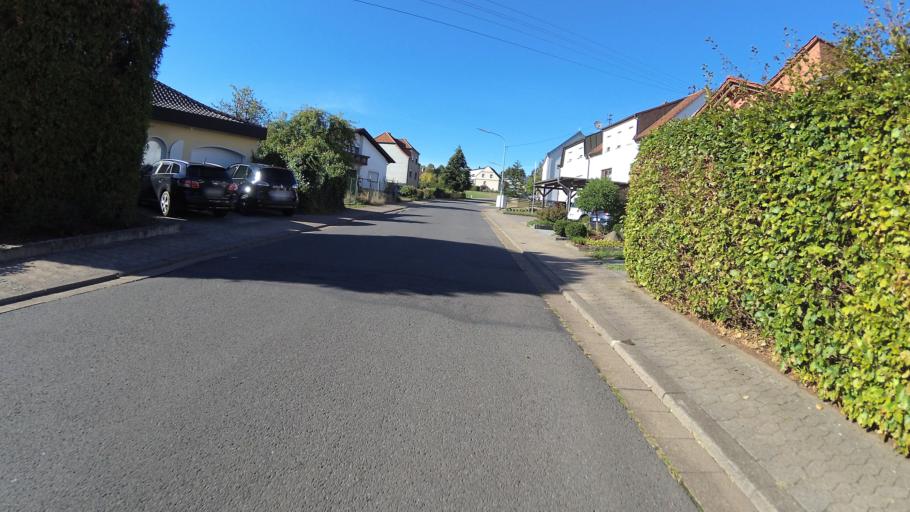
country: DE
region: Saarland
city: Eppelborn
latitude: 49.4112
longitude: 6.9624
